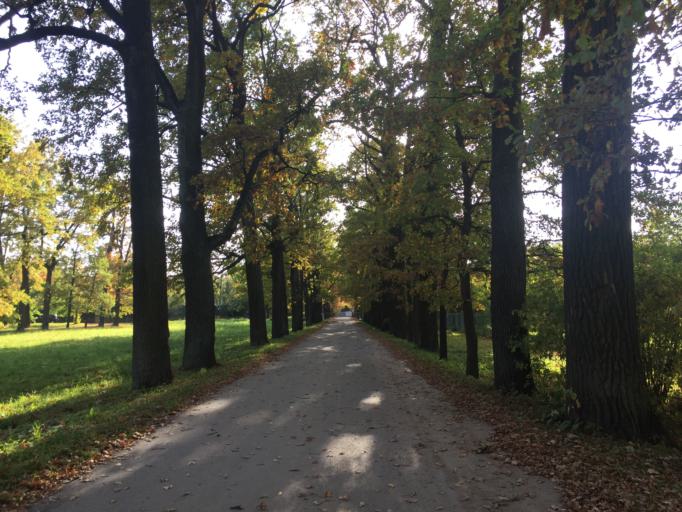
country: RU
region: St.-Petersburg
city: Pushkin
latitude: 59.7164
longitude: 30.3864
